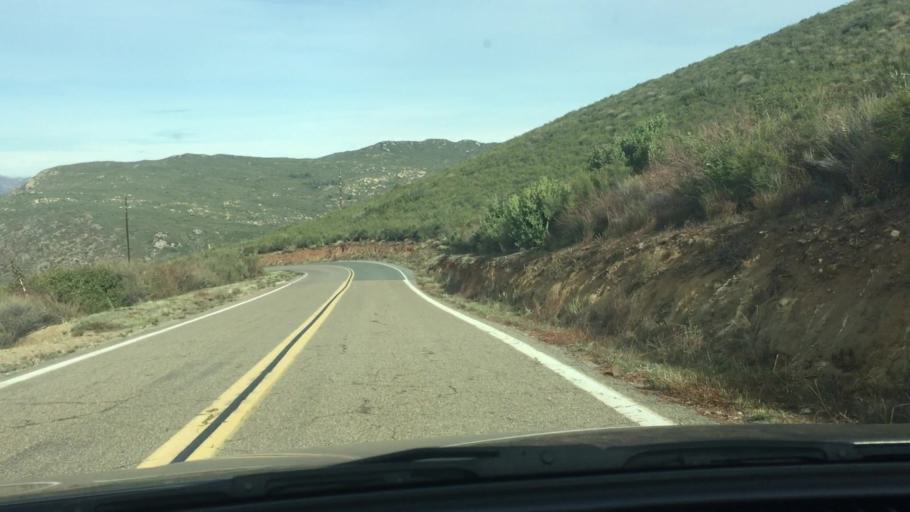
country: US
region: California
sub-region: San Diego County
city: Descanso
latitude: 32.8884
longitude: -116.6490
